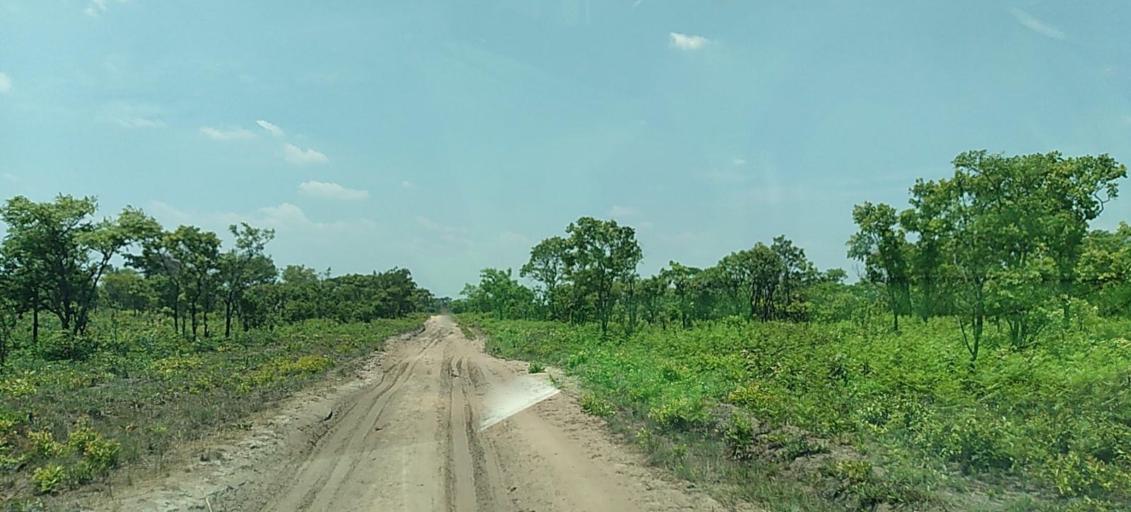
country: CD
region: Katanga
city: Kolwezi
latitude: -11.3369
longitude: 25.2232
